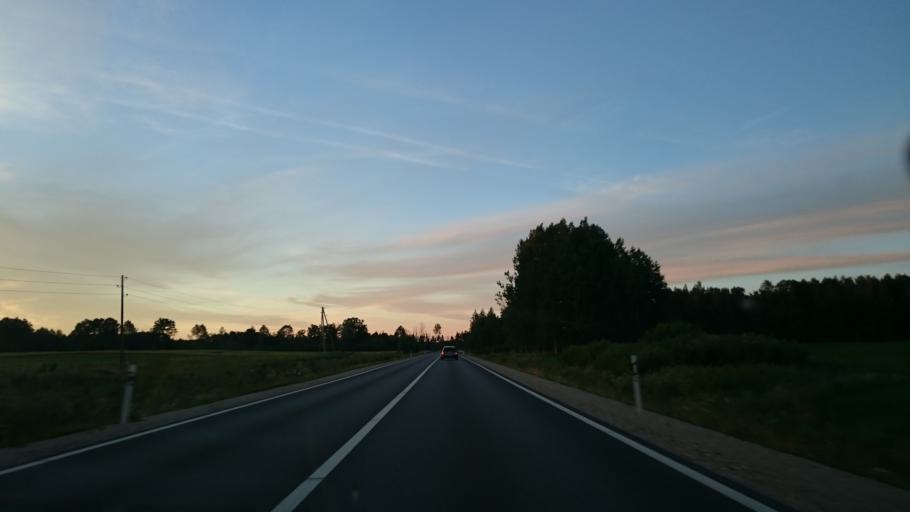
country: LV
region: Dobeles Rajons
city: Dobele
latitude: 56.7141
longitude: 23.1894
